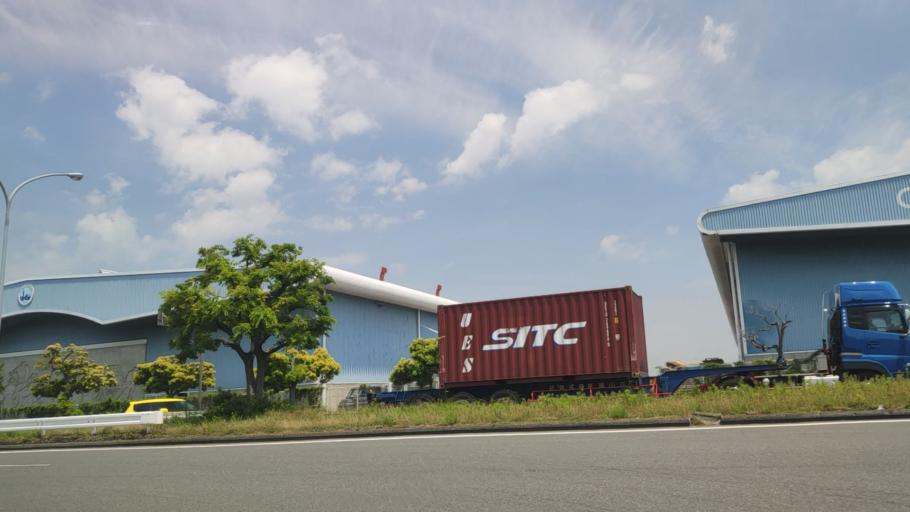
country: JP
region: Kanagawa
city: Yokohama
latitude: 35.4286
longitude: 139.6766
